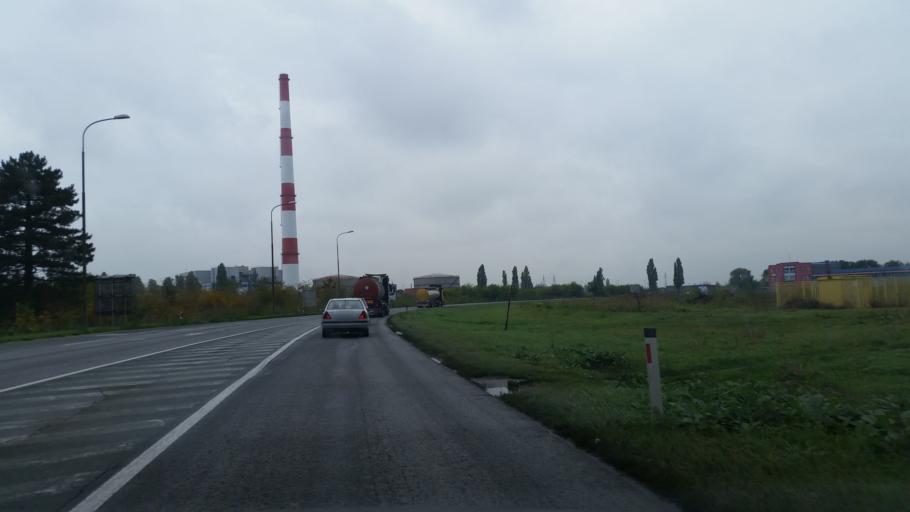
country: RS
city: Ecka
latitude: 45.3523
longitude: 20.4192
